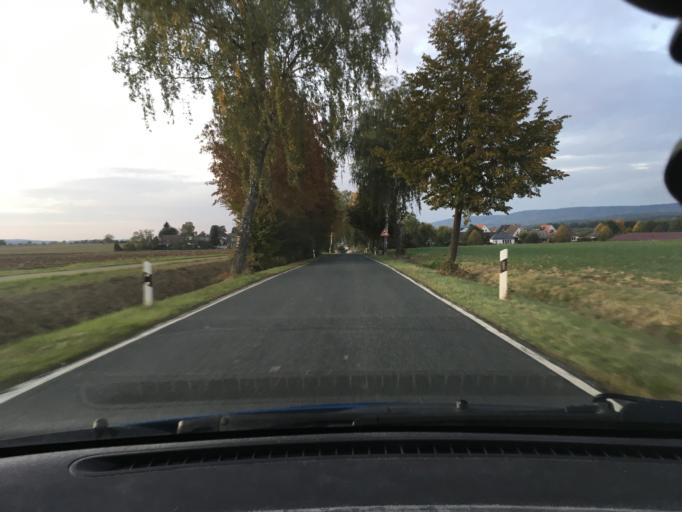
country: DE
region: Lower Saxony
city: Messenkamp
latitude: 52.2153
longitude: 9.3971
